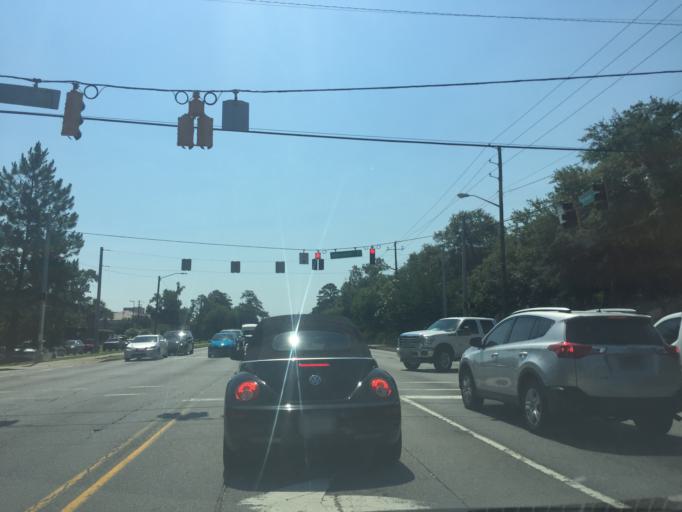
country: US
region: Georgia
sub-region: Chatham County
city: Savannah
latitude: 32.0277
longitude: -81.1063
